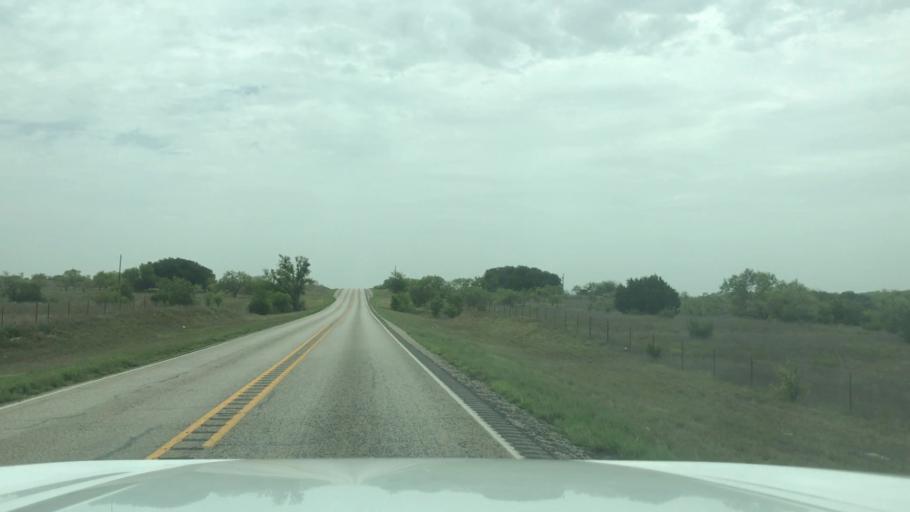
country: US
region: Texas
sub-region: Hamilton County
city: Hico
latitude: 32.0522
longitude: -98.1681
